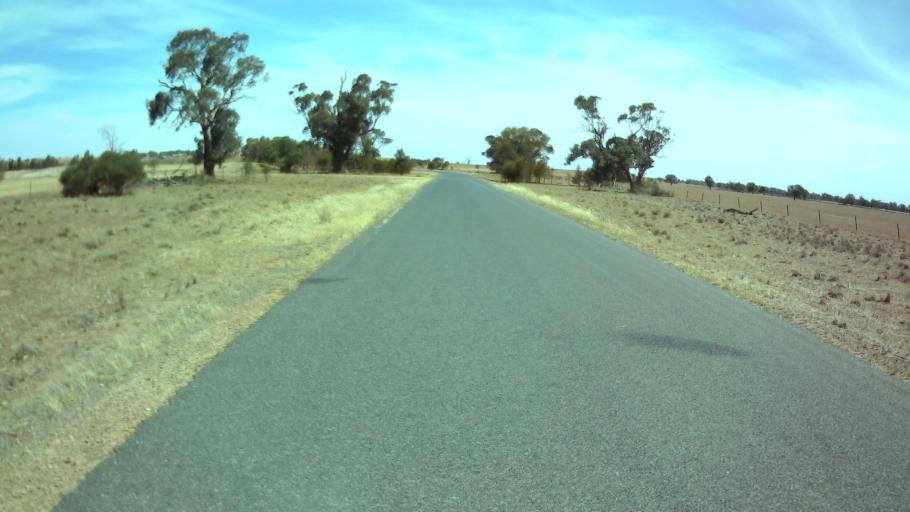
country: AU
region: New South Wales
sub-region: Weddin
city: Grenfell
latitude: -33.8853
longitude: 147.7421
